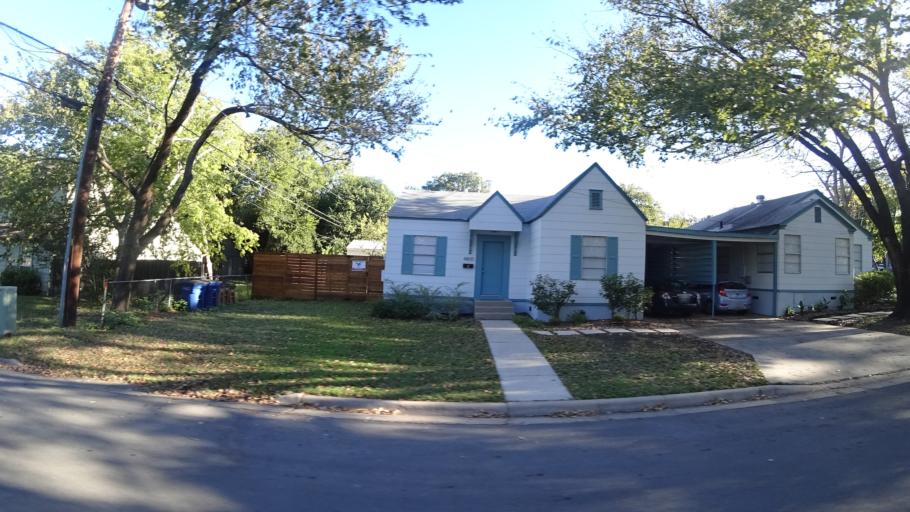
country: US
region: Texas
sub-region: Travis County
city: Austin
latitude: 30.3106
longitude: -97.7216
